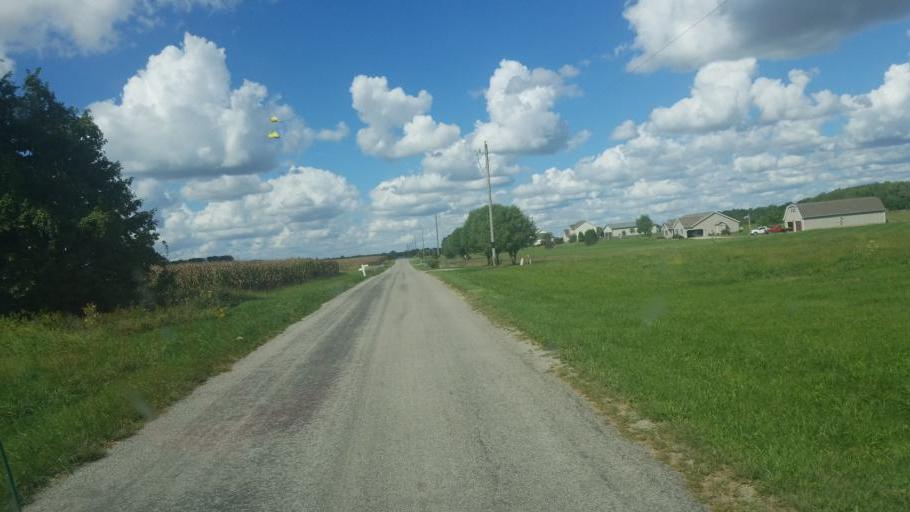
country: US
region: Ohio
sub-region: Union County
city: Richwood
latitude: 40.4658
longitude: -83.4960
